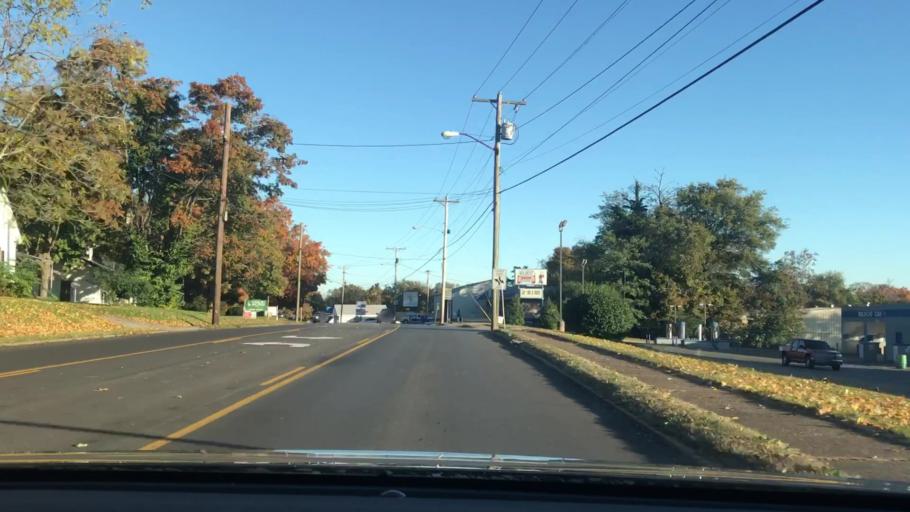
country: US
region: Kentucky
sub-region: Simpson County
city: Franklin
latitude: 36.7120
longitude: -86.5763
